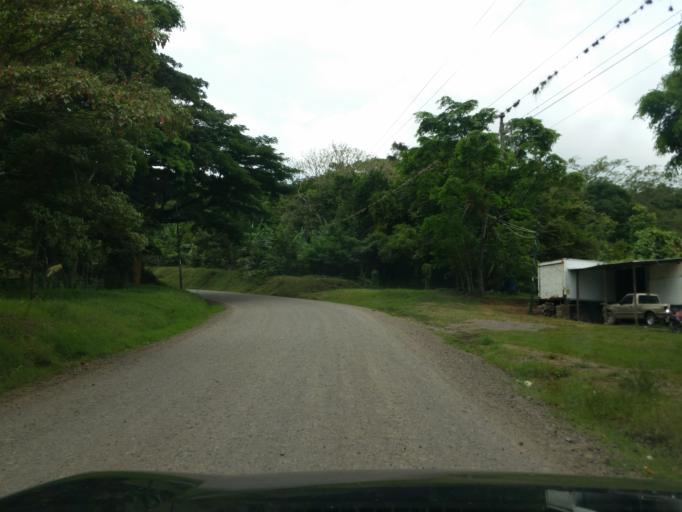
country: NI
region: Matagalpa
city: San Ramon
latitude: 12.9348
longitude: -85.8587
